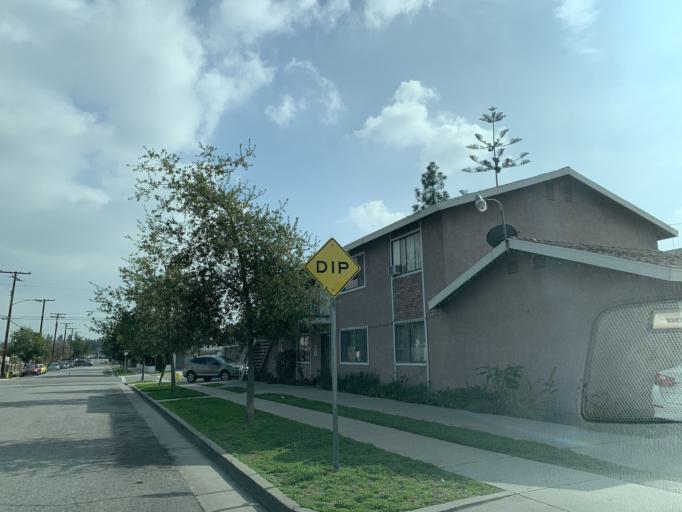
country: US
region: California
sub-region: Los Angeles County
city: Azusa
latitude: 34.1262
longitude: -117.9056
